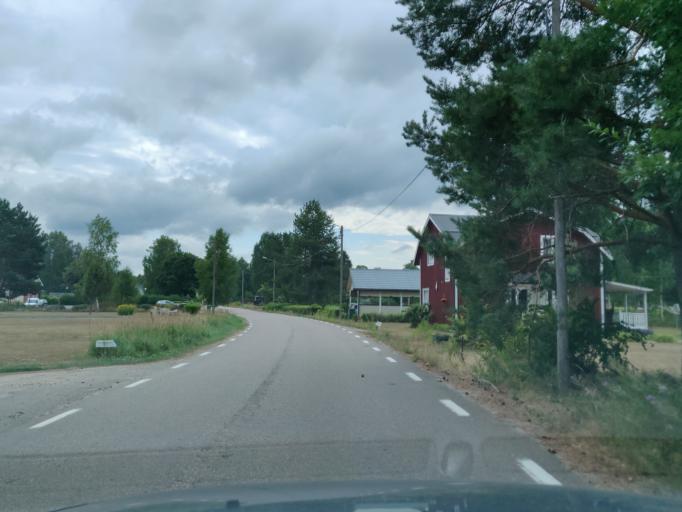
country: SE
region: Vaermland
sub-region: Munkfors Kommun
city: Munkfors
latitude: 59.8803
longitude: 13.5594
